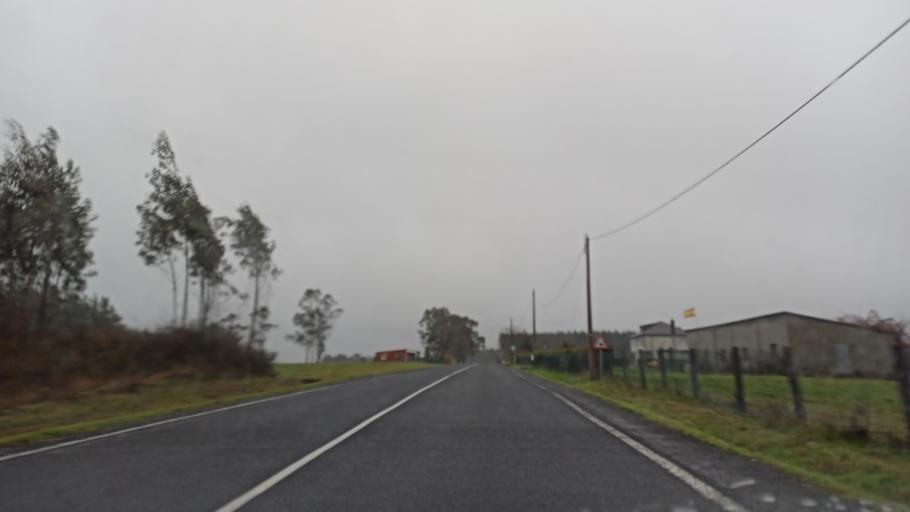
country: ES
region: Galicia
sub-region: Provincia da Coruna
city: Coiros
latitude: 43.1789
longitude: -8.1203
